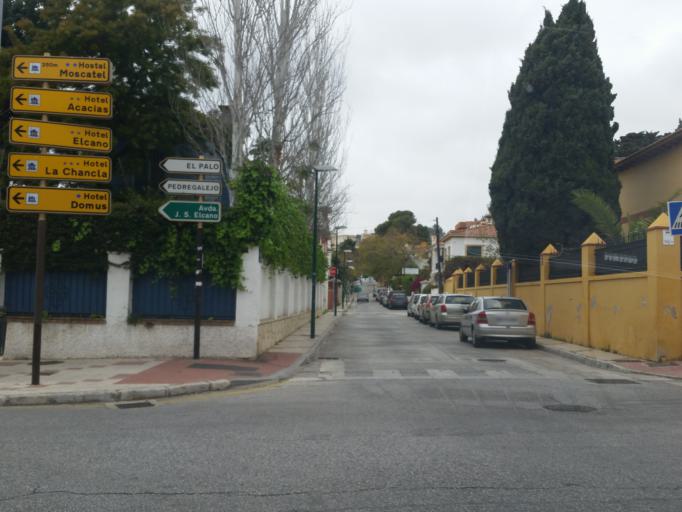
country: ES
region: Andalusia
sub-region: Provincia de Malaga
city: Malaga
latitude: 36.7255
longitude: -4.3661
